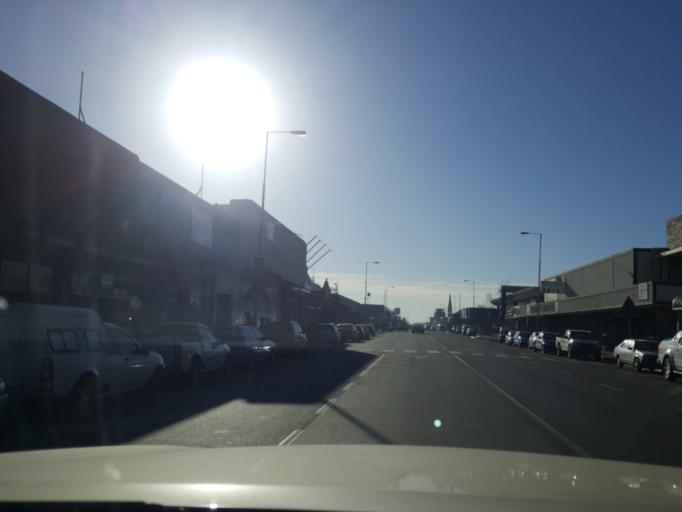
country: ZA
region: North-West
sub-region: Ngaka Modiri Molema District Municipality
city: Zeerust
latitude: -25.5457
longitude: 26.0771
